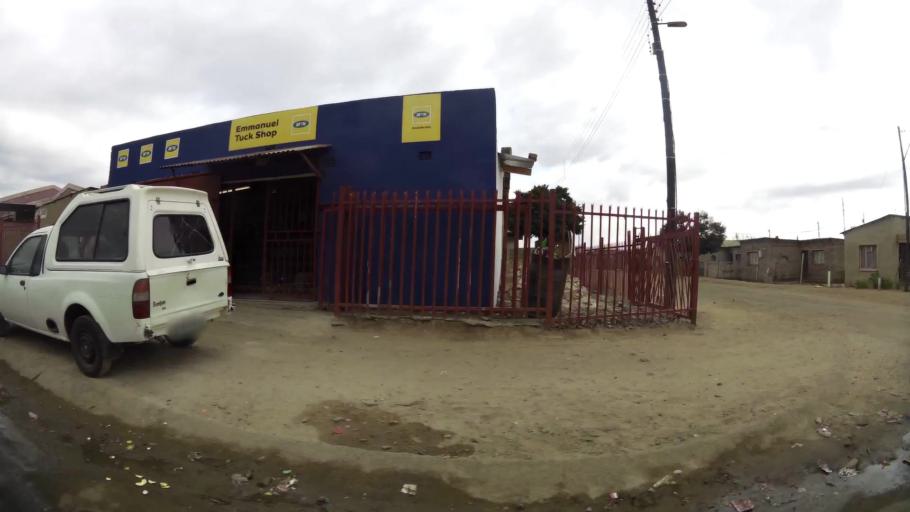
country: ZA
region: Orange Free State
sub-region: Fezile Dabi District Municipality
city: Kroonstad
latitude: -27.6475
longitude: 27.1957
